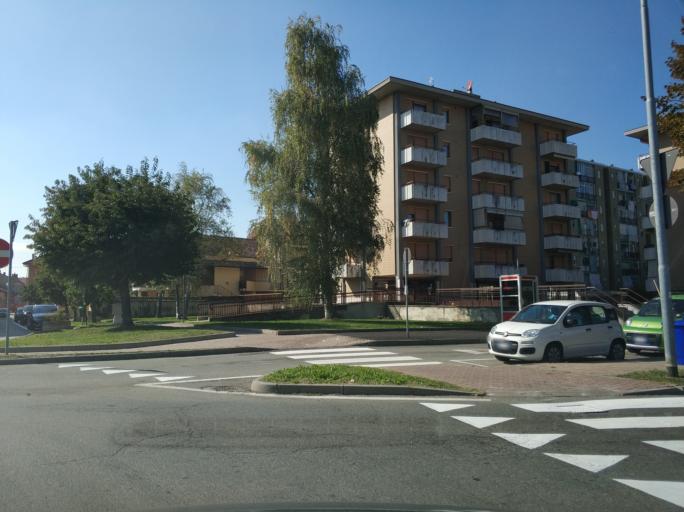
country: IT
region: Piedmont
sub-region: Provincia di Torino
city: Borgaro Torinese
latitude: 45.1524
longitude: 7.6595
